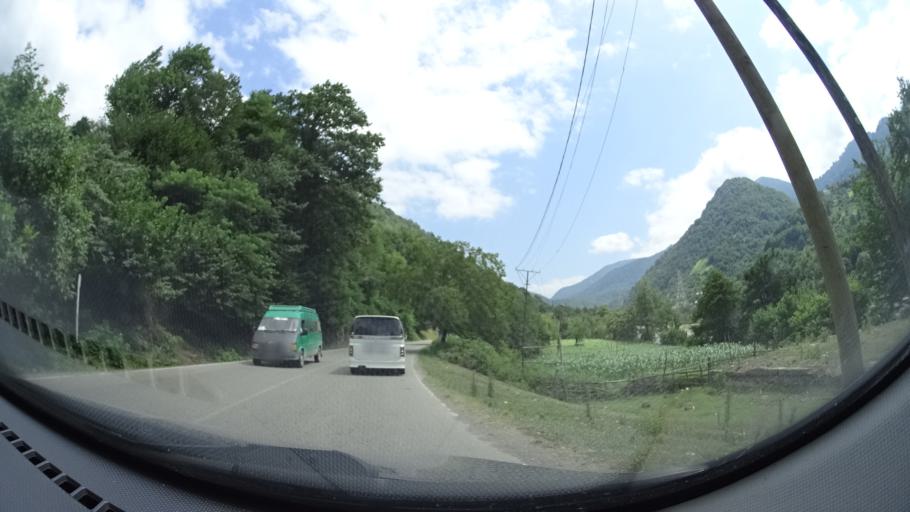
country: TR
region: Artvin
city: Camili
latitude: 41.5656
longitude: 41.8336
